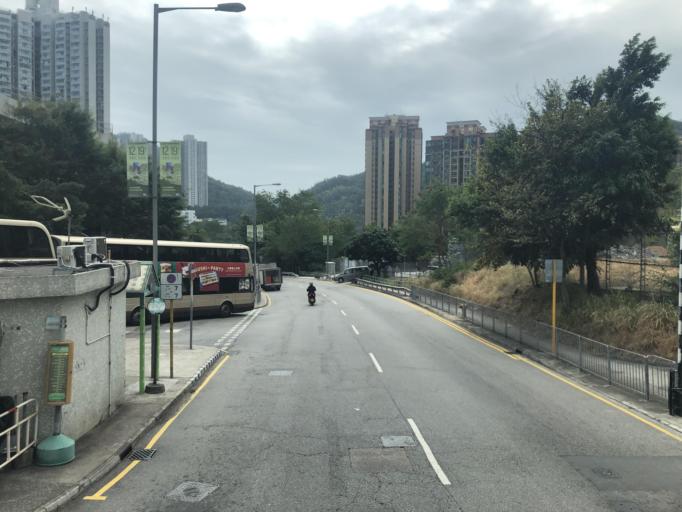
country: HK
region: Tsuen Wan
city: Tsuen Wan
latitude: 22.3556
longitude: 114.0974
